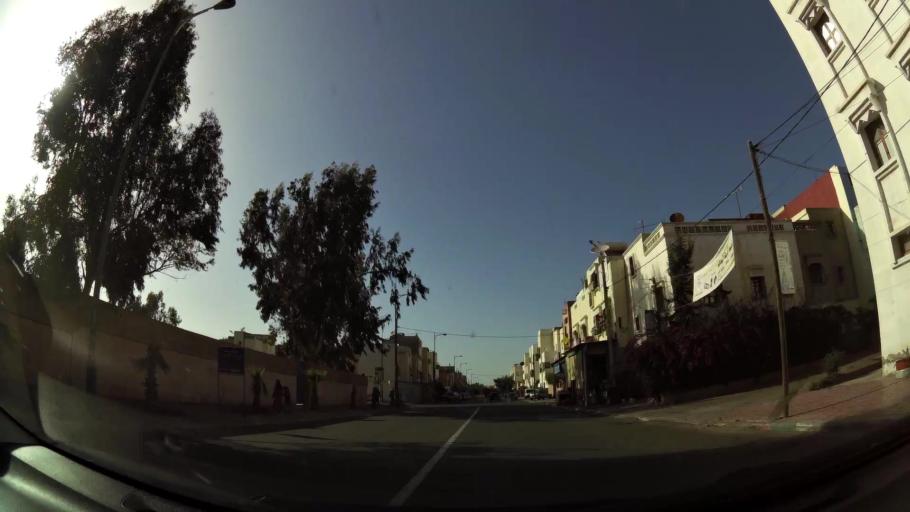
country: MA
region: Souss-Massa-Draa
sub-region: Inezgane-Ait Mellou
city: Inezgane
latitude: 30.3659
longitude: -9.5282
